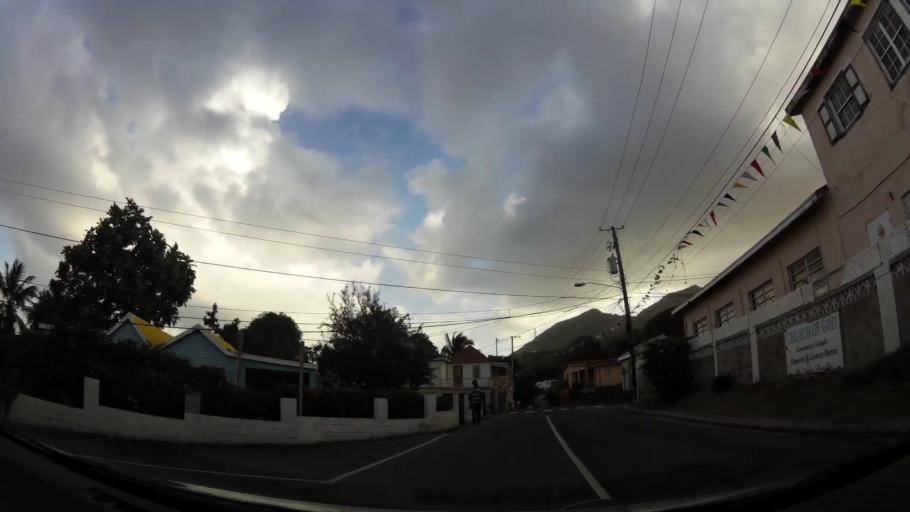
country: KN
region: Saint James Windwa
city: Newcastle
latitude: 17.1846
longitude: -62.5594
